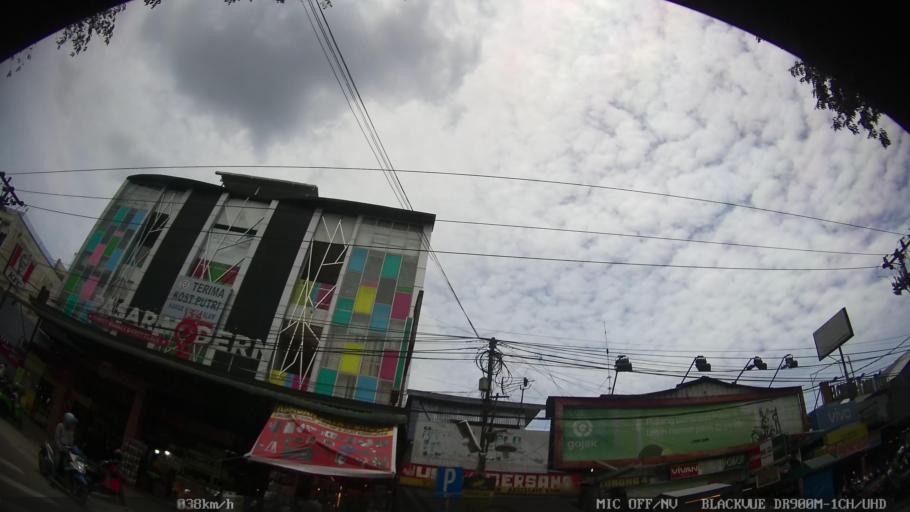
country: ID
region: North Sumatra
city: Medan
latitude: 3.5604
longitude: 98.6619
